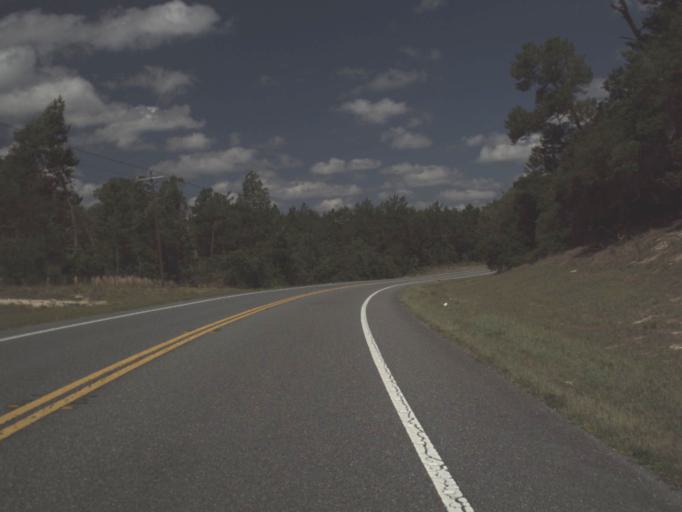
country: US
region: Florida
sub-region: Lake County
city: Astor
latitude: 29.1671
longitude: -81.6506
